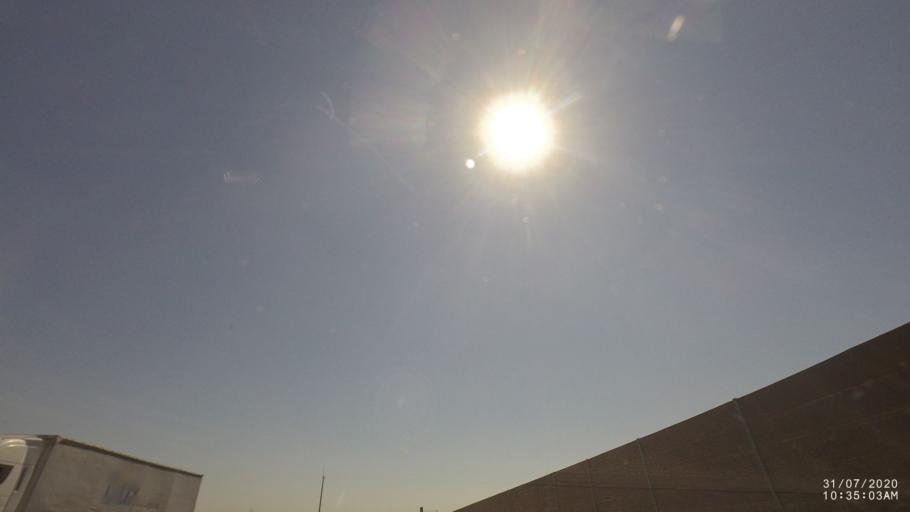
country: SK
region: Trnavsky
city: Samorin
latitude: 48.0137
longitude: 17.4475
